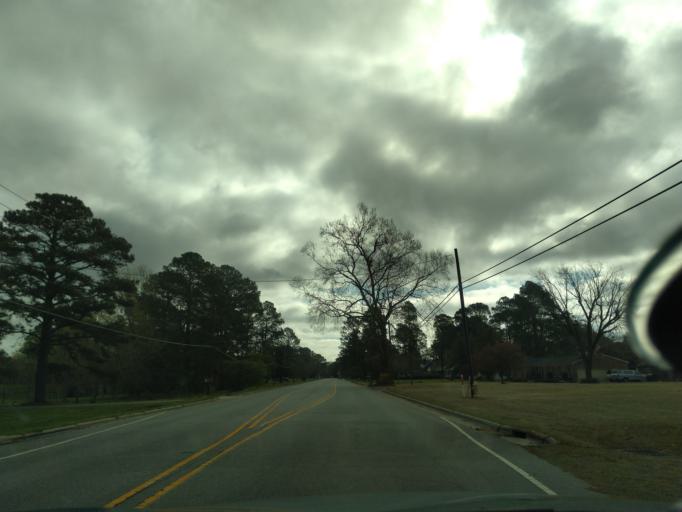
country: US
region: North Carolina
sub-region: Chowan County
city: Edenton
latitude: 36.0569
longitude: -76.6387
